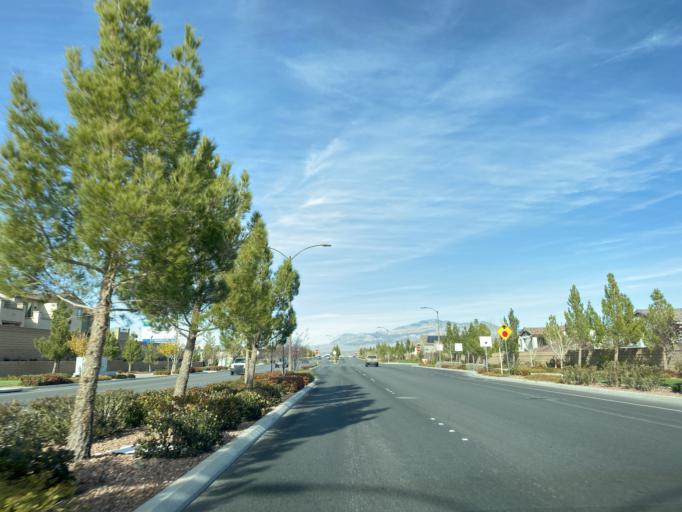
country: US
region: Nevada
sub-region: Clark County
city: Summerlin South
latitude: 36.3094
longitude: -115.3149
